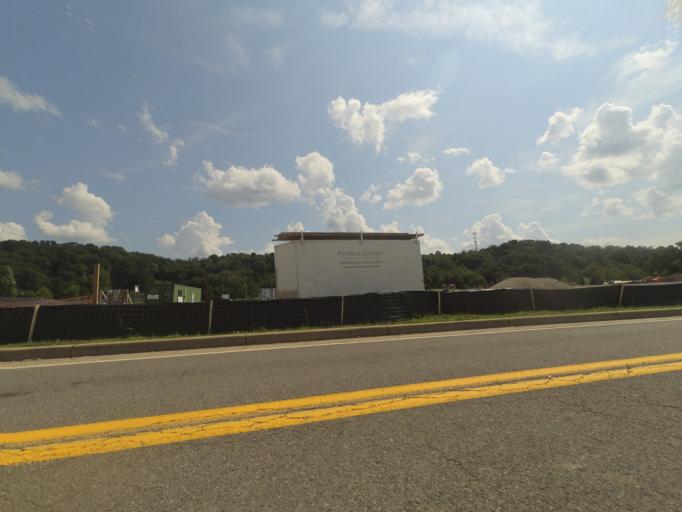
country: US
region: West Virginia
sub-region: Cabell County
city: Huntington
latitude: 38.3939
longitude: -82.4228
